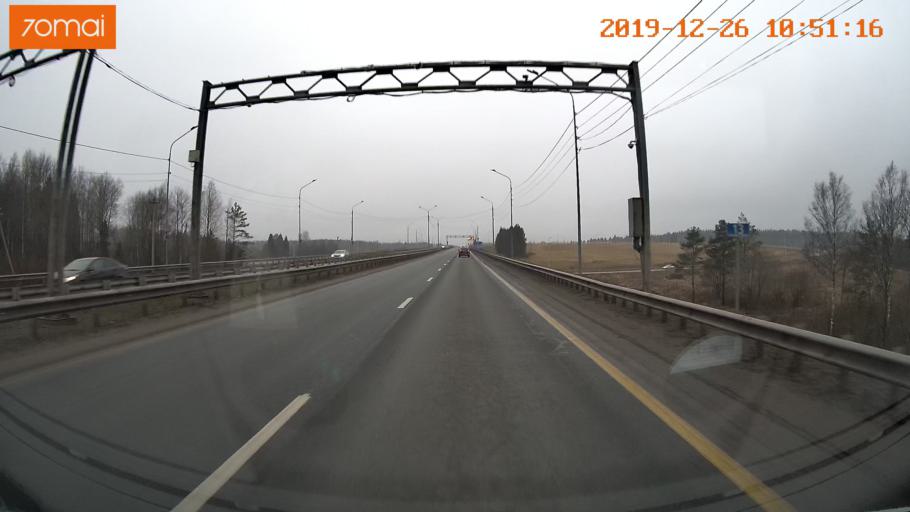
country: RU
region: Vologda
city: Molochnoye
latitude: 59.2044
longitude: 39.6664
